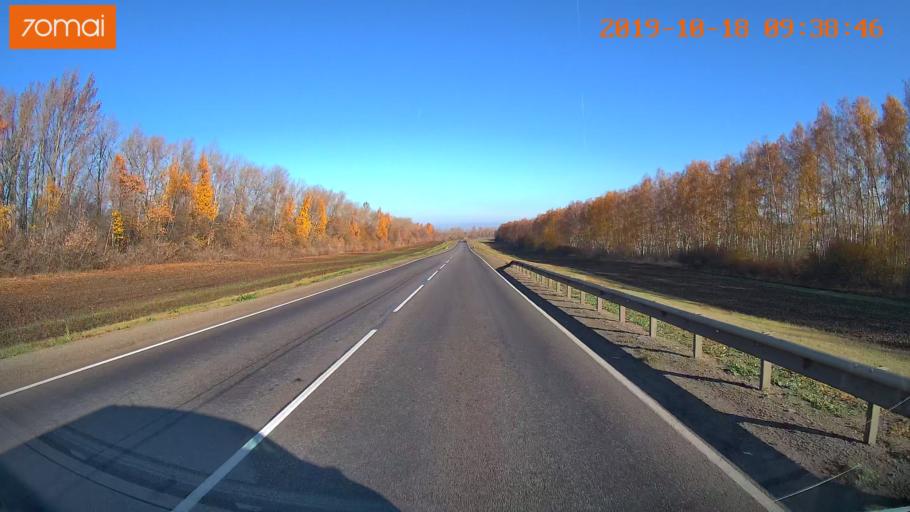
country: RU
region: Tula
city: Yefremov
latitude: 53.2428
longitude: 38.1358
